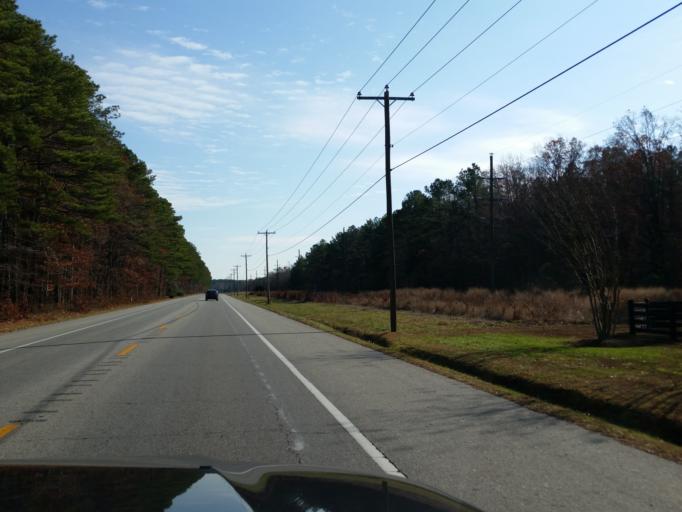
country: US
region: Maryland
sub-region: Talbot County
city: Saint Michaels
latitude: 38.7641
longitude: -76.1985
